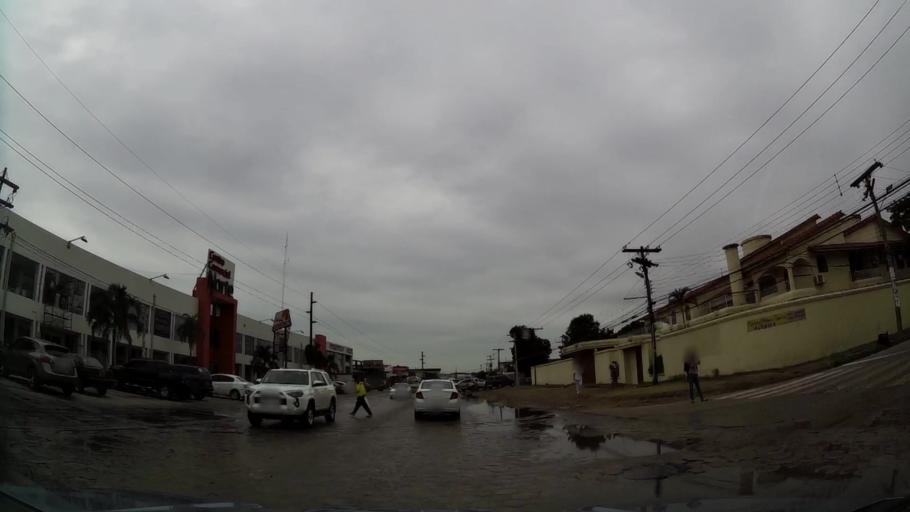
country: BO
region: Santa Cruz
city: Santa Cruz de la Sierra
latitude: -17.7614
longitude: -63.1660
